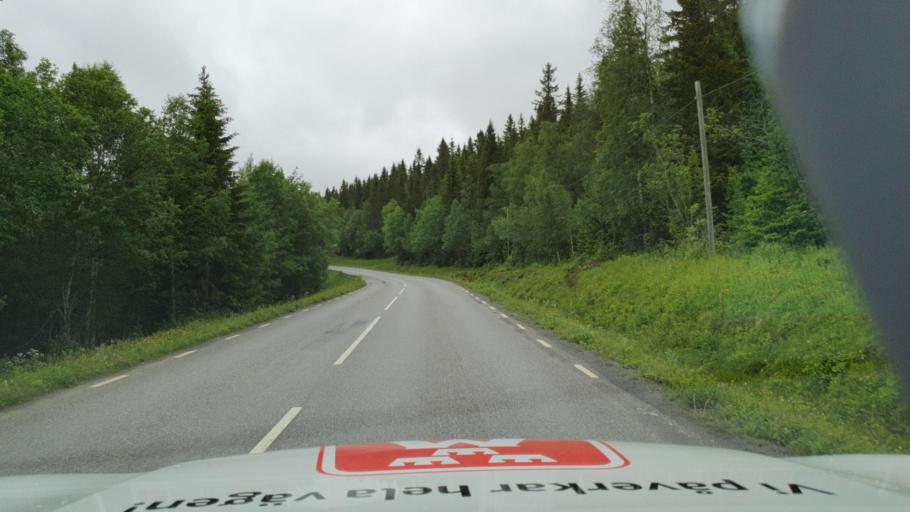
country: SE
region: Jaemtland
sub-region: Are Kommun
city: Are
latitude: 63.5004
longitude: 13.1650
